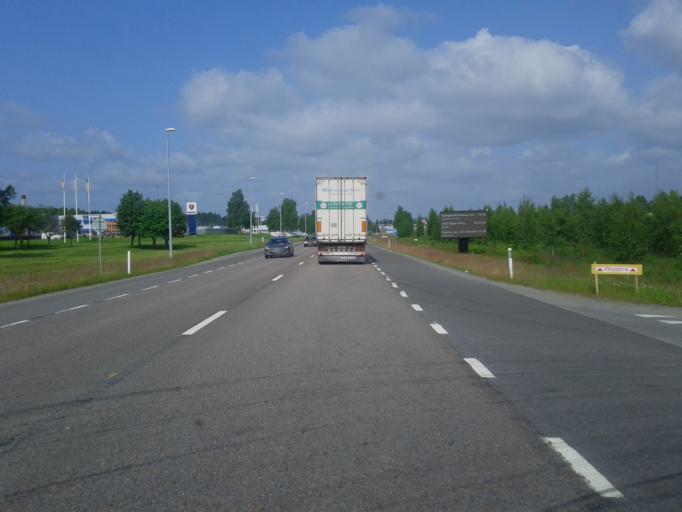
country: SE
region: Vaesterbotten
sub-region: Skelleftea Kommun
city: Skelleftea
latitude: 64.7320
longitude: 20.9729
